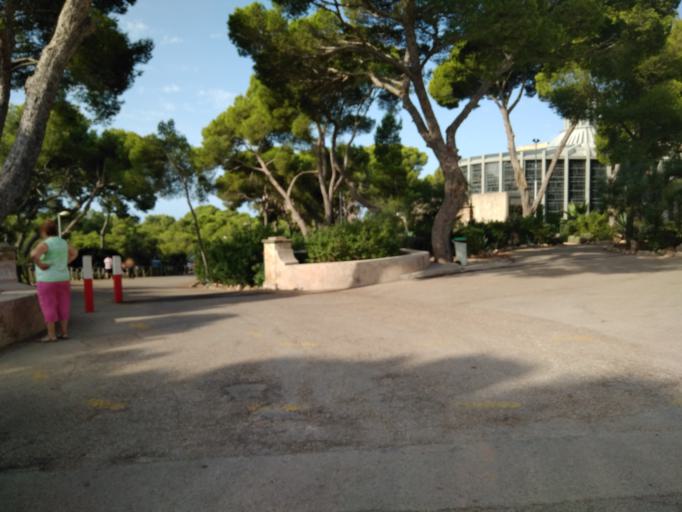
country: ES
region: Balearic Islands
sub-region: Illes Balears
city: s'Arenal
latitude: 39.5196
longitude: 2.7514
